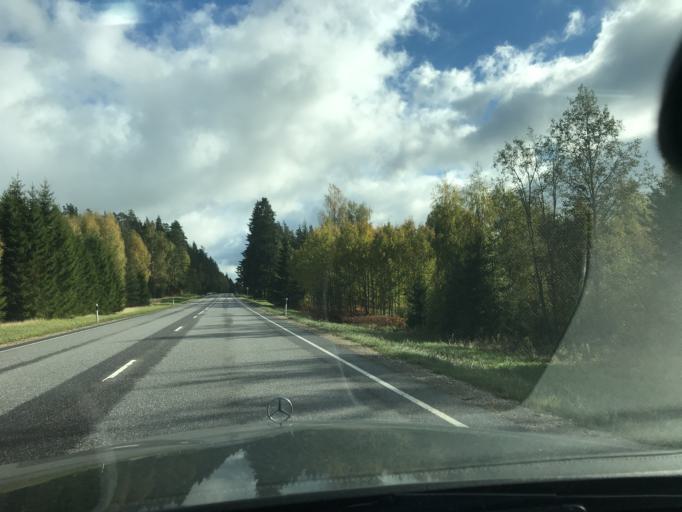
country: EE
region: Vorumaa
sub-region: Voru linn
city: Voru
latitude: 57.7667
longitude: 27.1778
